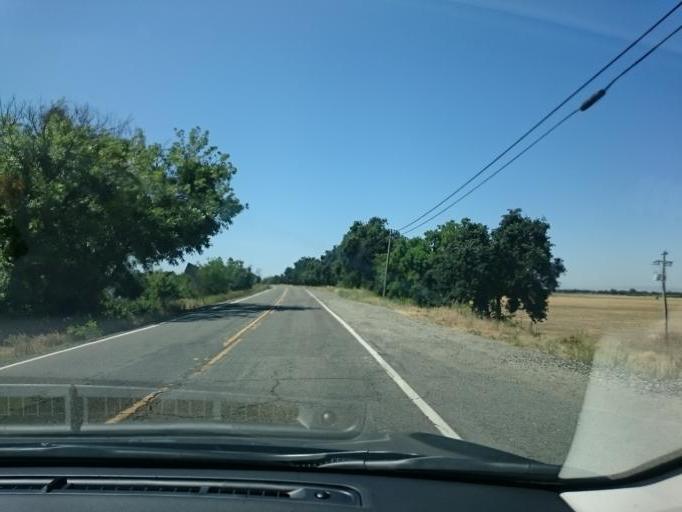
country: US
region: California
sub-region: Yolo County
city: West Sacramento
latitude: 38.5019
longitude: -121.5603
